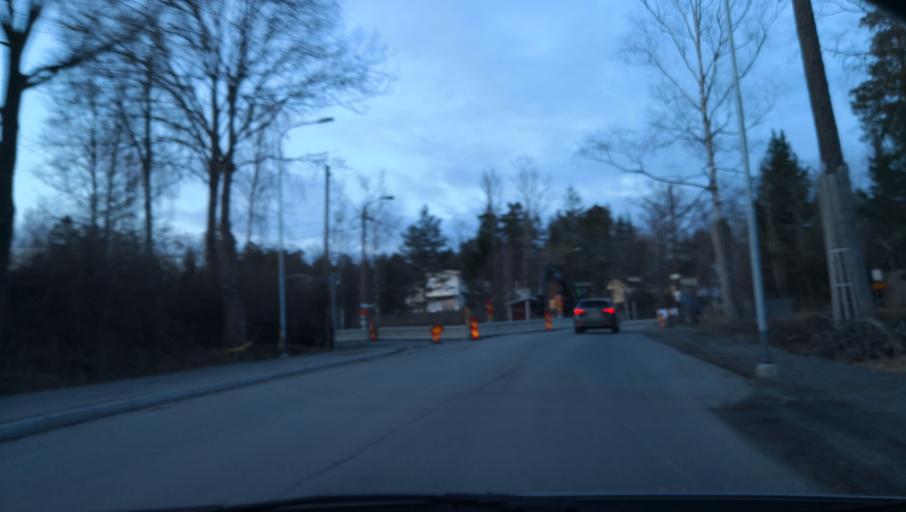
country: SE
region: Stockholm
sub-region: Nacka Kommun
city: Kummelnas
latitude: 59.3506
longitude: 18.2891
